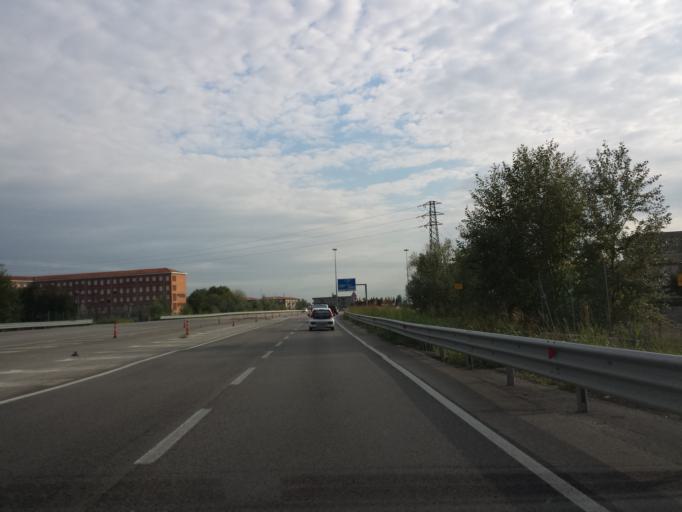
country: IT
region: Veneto
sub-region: Provincia di Rovigo
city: Rovigo
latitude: 45.0791
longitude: 11.8078
